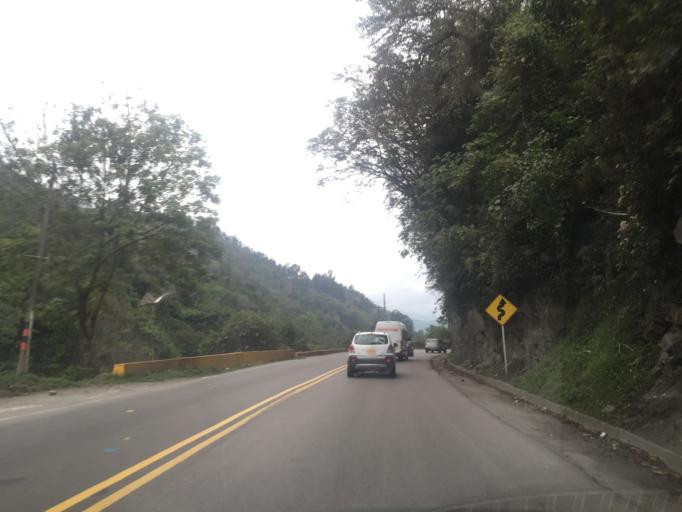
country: CO
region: Tolima
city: Cajamarca
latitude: 4.4346
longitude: -75.4519
